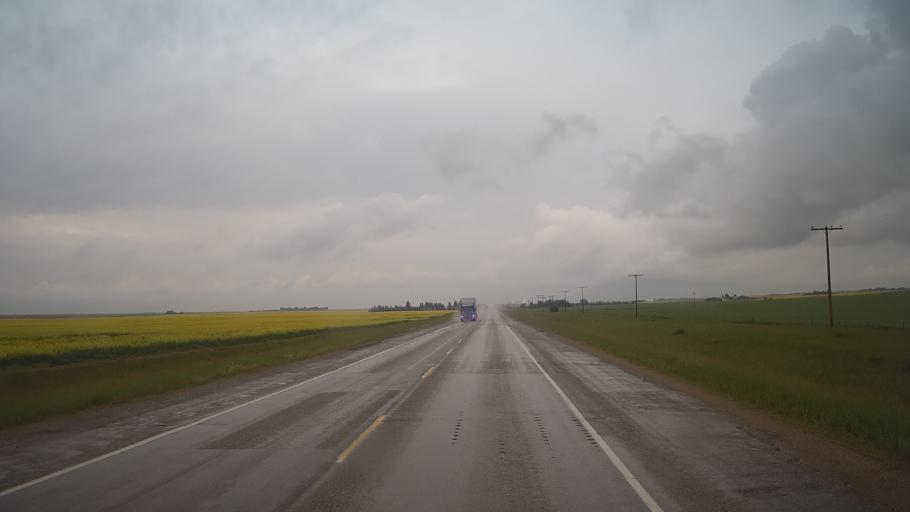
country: CA
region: Saskatchewan
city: Unity
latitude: 52.4349
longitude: -109.0180
